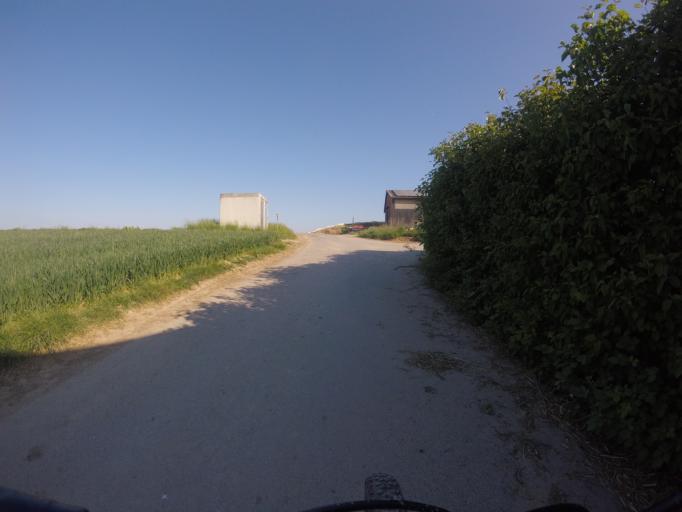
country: DE
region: Baden-Wuerttemberg
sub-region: Regierungsbezirk Stuttgart
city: Aspach
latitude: 48.9796
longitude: 9.4011
